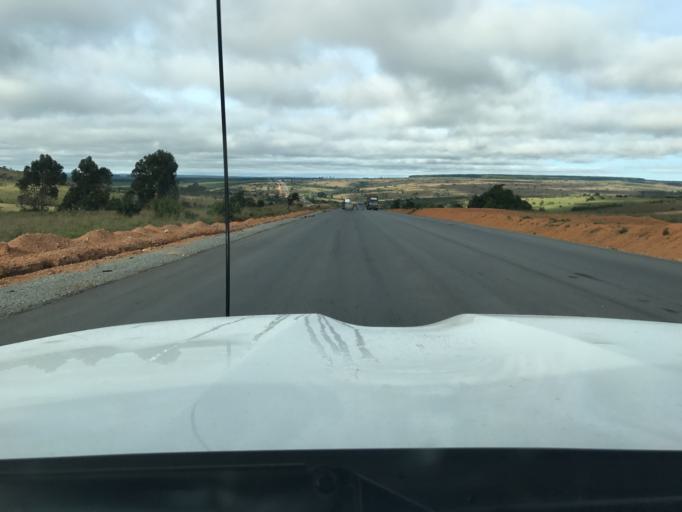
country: TZ
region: Iringa
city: Makungu
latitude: -8.3342
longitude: 35.2565
